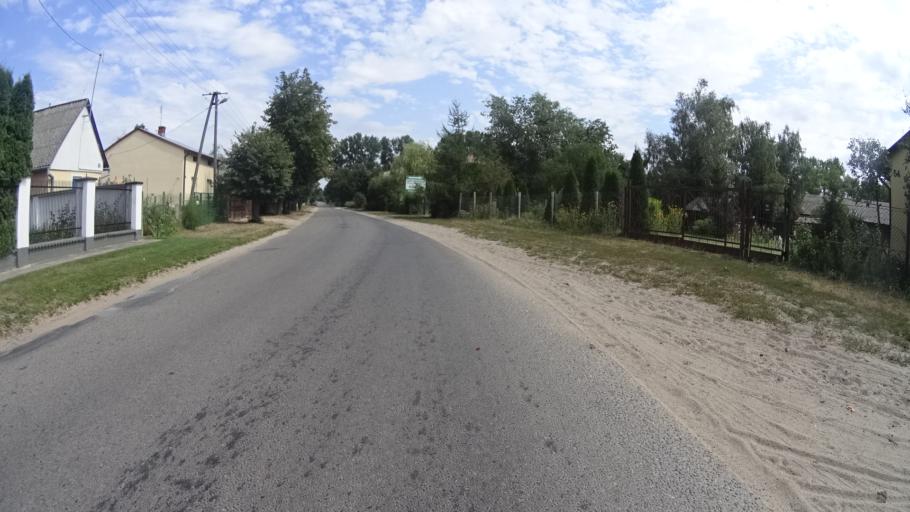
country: PL
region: Masovian Voivodeship
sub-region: Powiat bialobrzeski
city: Wysmierzyce
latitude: 51.6515
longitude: 20.7873
